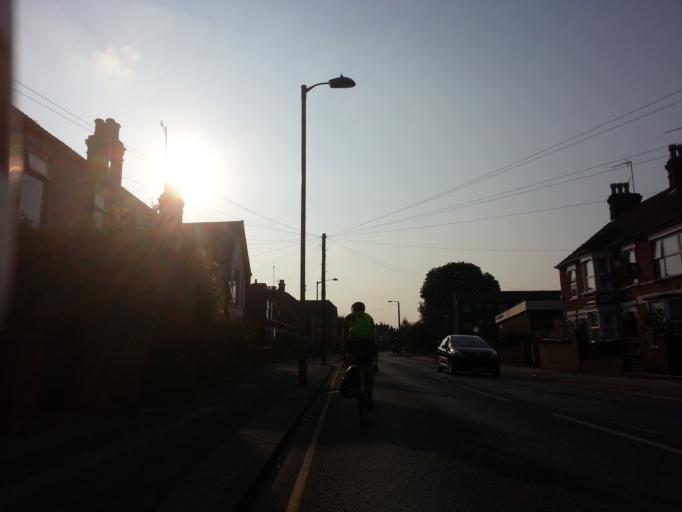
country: GB
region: England
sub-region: Suffolk
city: Ipswich
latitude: 52.0638
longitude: 1.1356
